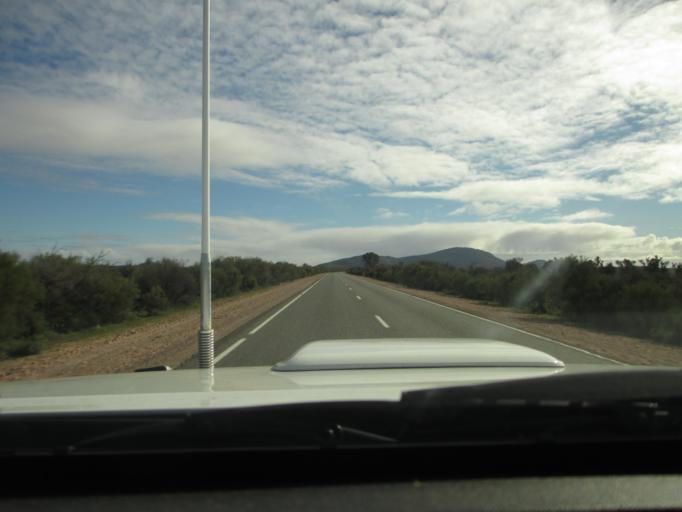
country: AU
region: South Australia
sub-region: Flinders Ranges
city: Quorn
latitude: -31.8328
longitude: 138.3864
